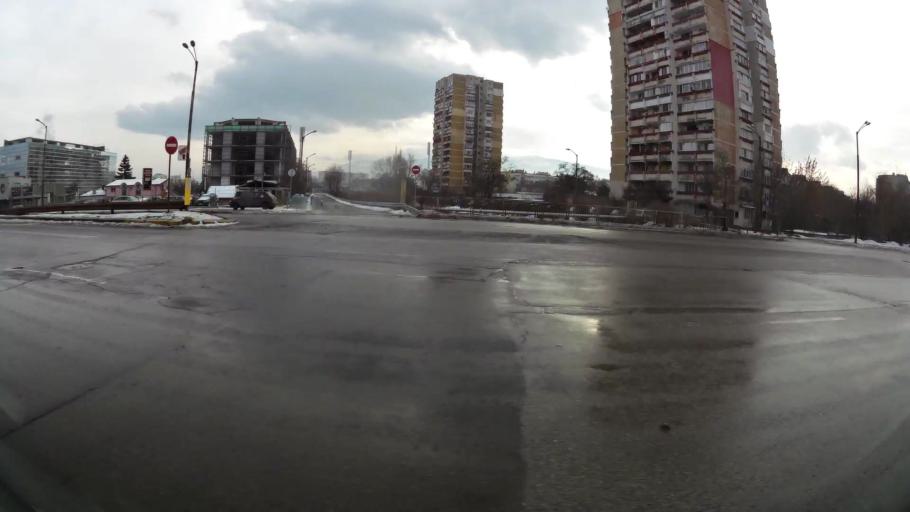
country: BG
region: Sofia-Capital
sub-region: Stolichna Obshtina
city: Sofia
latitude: 42.7105
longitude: 23.3640
